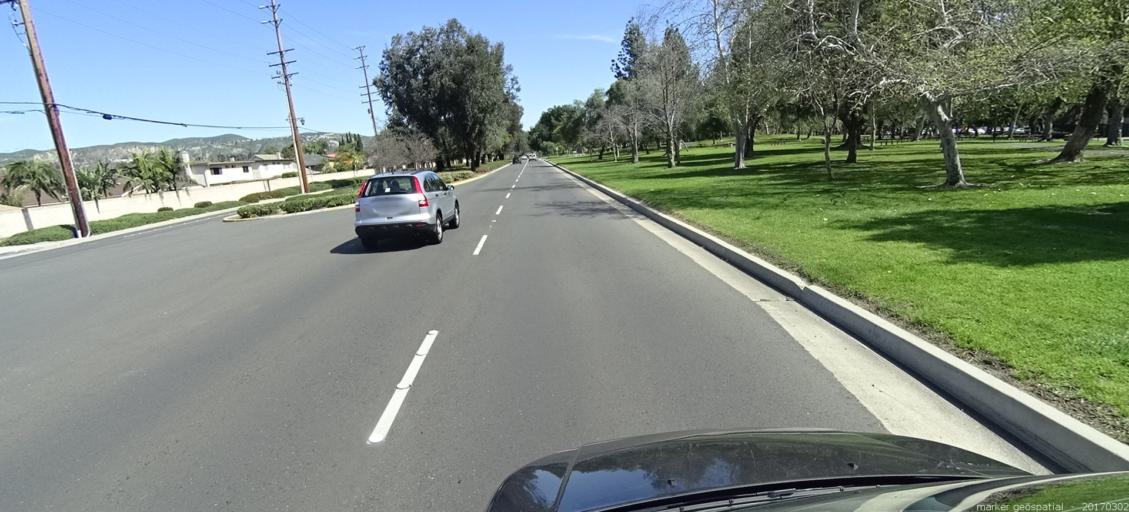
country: US
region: California
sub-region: Orange County
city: Yorba Linda
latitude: 33.8711
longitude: -117.7655
